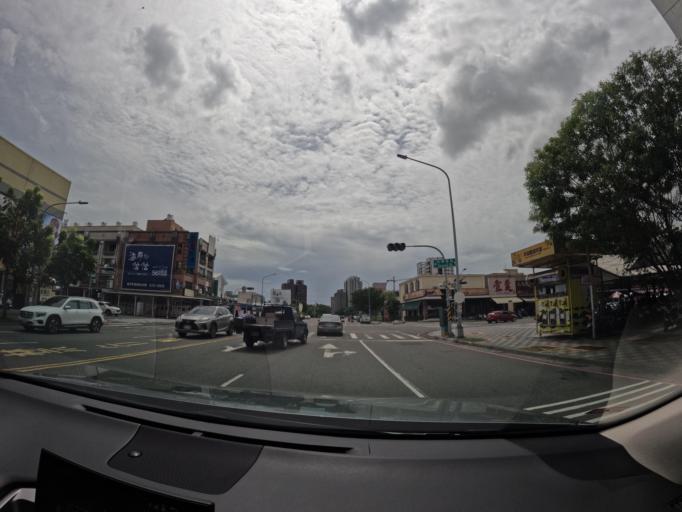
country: TW
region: Kaohsiung
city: Kaohsiung
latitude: 22.7276
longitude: 120.2902
